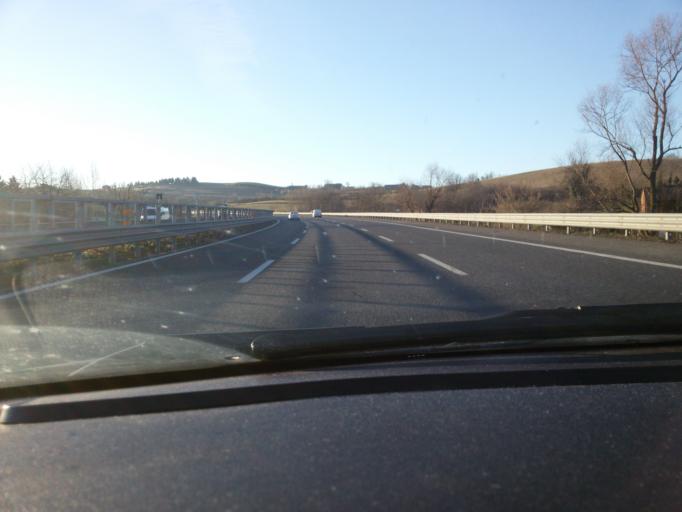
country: IT
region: Piedmont
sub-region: Provincia di Alessandria
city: Mirabello Monferrato
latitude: 45.0058
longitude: 8.5351
